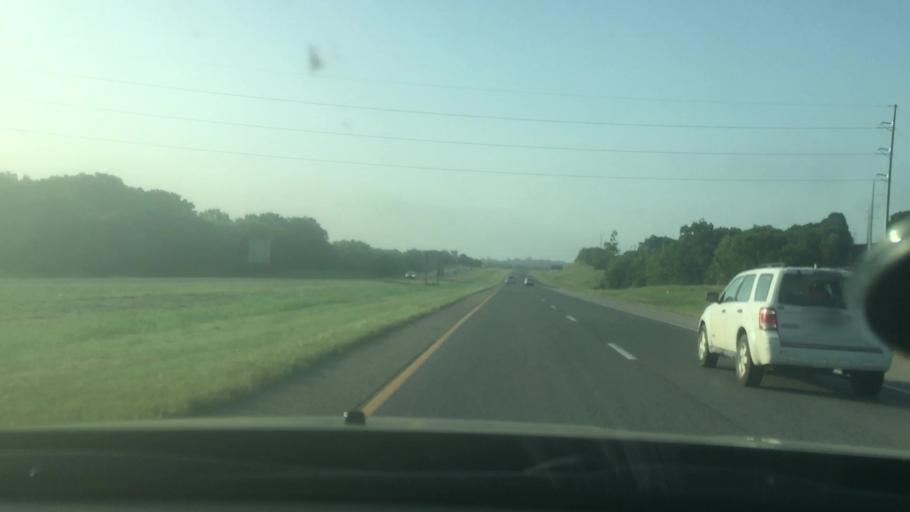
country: US
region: Oklahoma
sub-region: Pontotoc County
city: Ada
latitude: 34.7463
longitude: -96.6525
